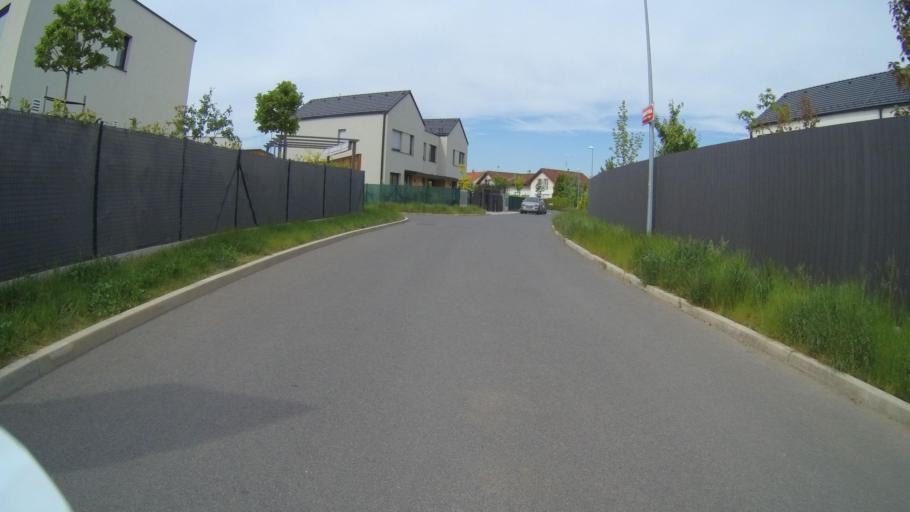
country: CZ
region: Central Bohemia
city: Libeznice
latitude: 50.1692
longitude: 14.4800
